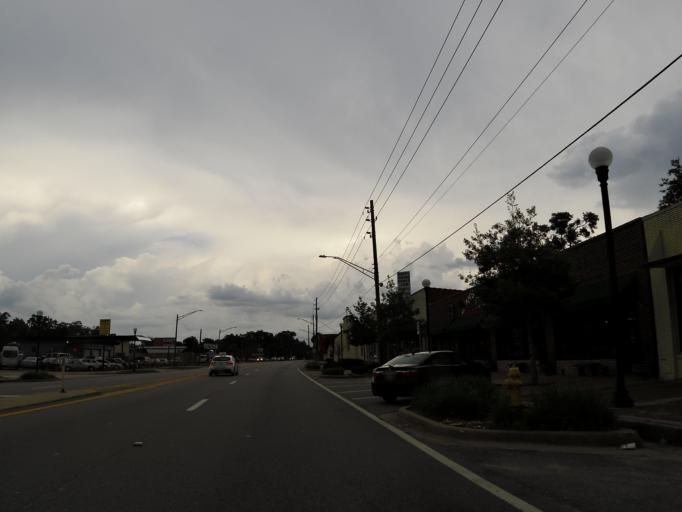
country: US
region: Florida
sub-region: Duval County
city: Jacksonville
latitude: 30.3031
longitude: -81.6335
